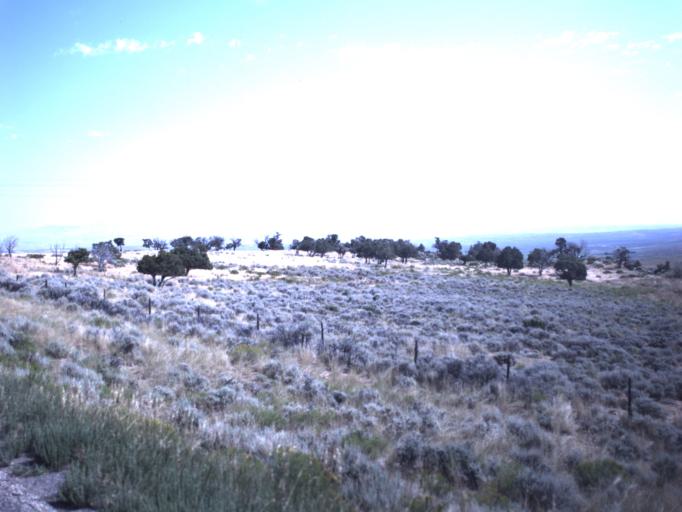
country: US
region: Utah
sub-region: Daggett County
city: Manila
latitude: 40.9806
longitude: -109.8376
